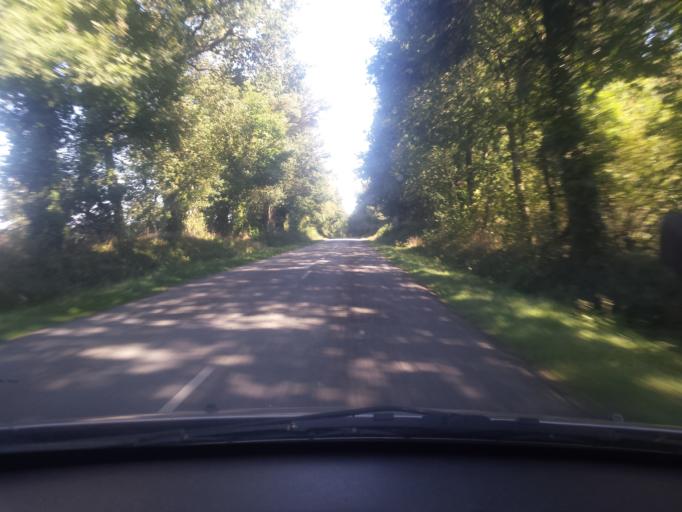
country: FR
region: Brittany
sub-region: Departement du Morbihan
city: Cleguerec
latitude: 48.0987
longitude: -3.0880
